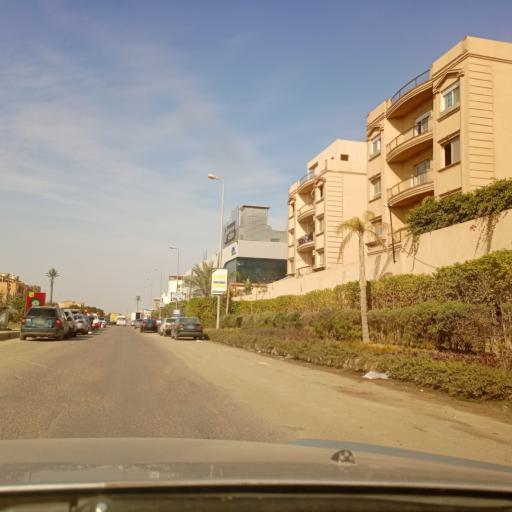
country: EG
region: Muhafazat al Qalyubiyah
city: Al Khankah
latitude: 30.0342
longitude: 31.4854
